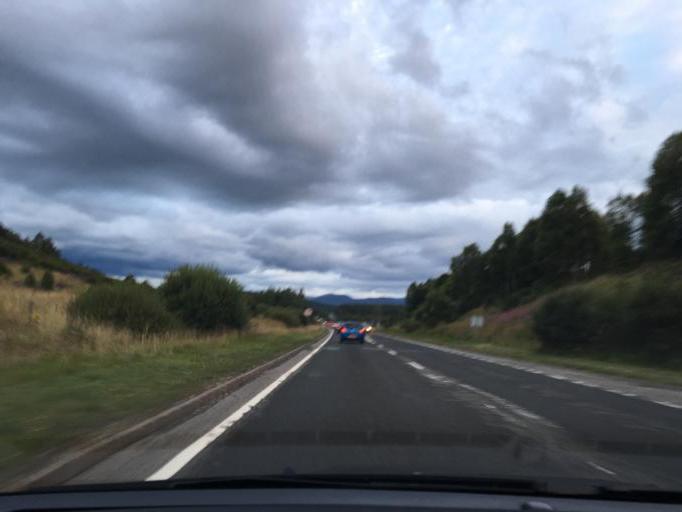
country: GB
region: Scotland
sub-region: Highland
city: Aviemore
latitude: 57.2841
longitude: -3.8388
